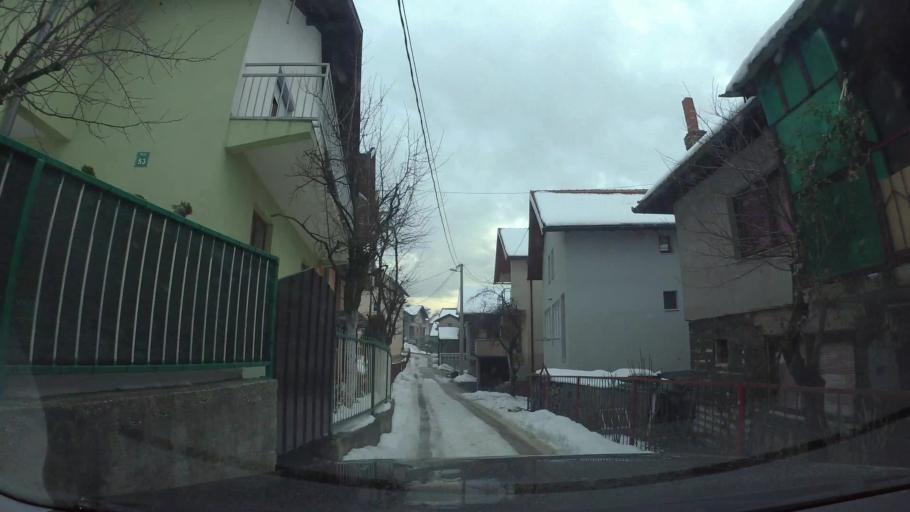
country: BA
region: Federation of Bosnia and Herzegovina
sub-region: Kanton Sarajevo
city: Sarajevo
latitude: 43.8601
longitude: 18.3515
